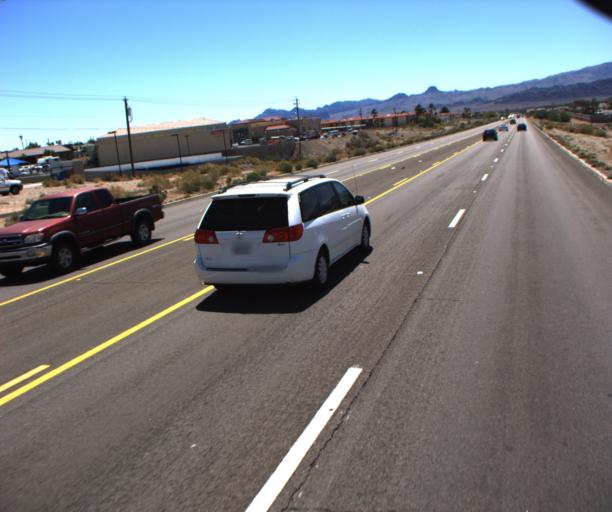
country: US
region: Arizona
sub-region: Mohave County
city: Lake Havasu City
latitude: 34.4907
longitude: -114.3494
